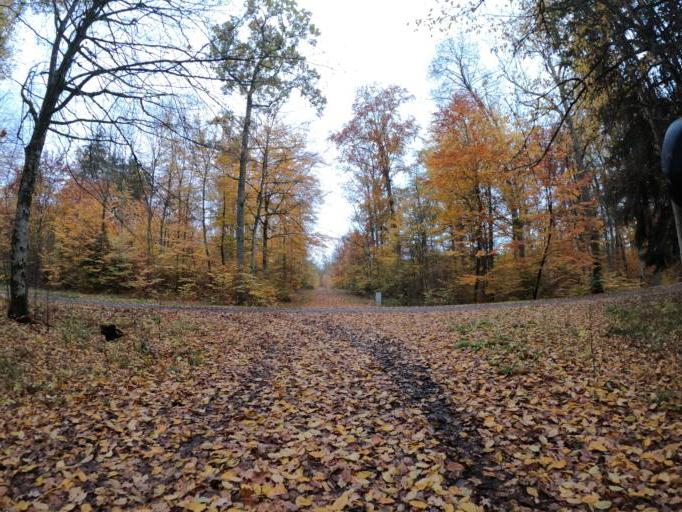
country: DE
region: Baden-Wuerttemberg
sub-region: Regierungsbezirk Stuttgart
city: Ehningen
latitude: 48.6421
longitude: 8.9481
